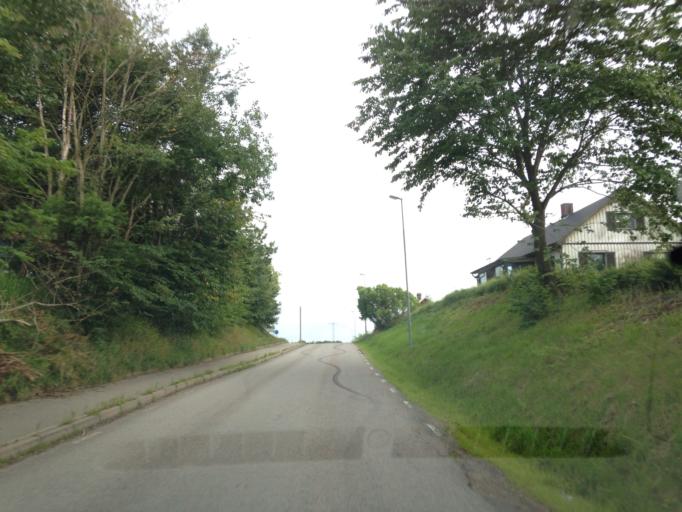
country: SE
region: Halland
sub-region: Varbergs Kommun
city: Tvaaker
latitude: 57.1238
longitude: 12.3923
